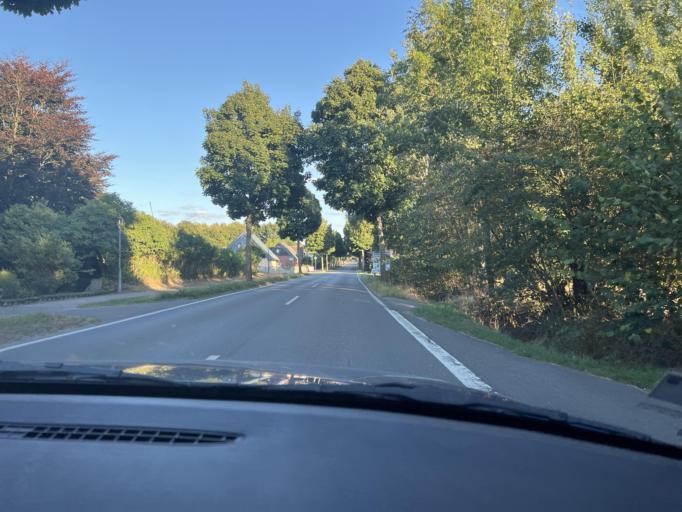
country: DE
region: Schleswig-Holstein
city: Hennstedt
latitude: 54.2876
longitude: 9.1518
